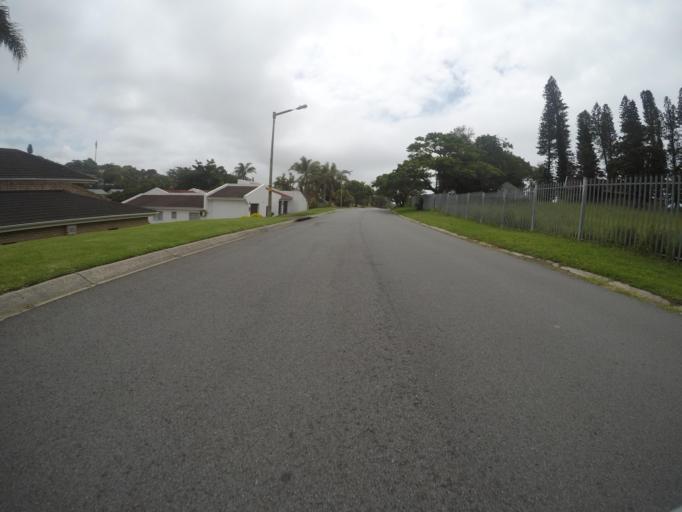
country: ZA
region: Eastern Cape
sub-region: Buffalo City Metropolitan Municipality
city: East London
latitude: -32.9924
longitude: 27.9355
